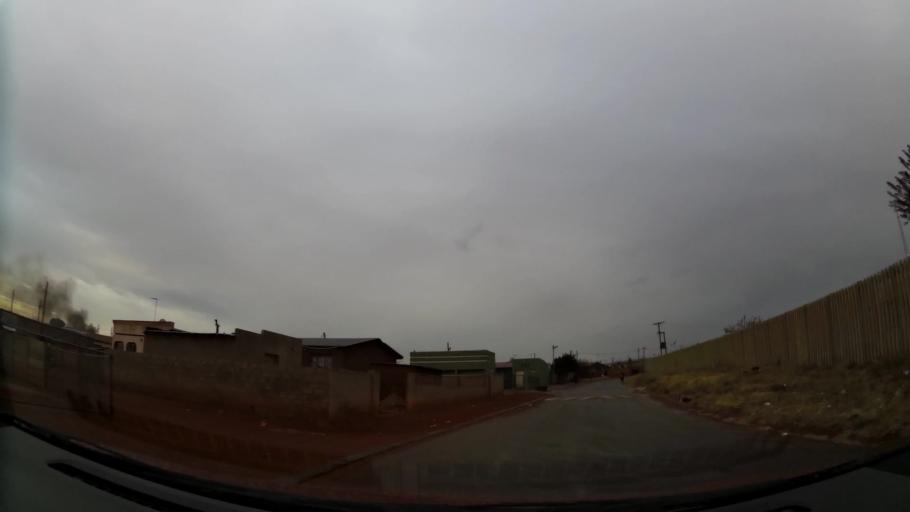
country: ZA
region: Gauteng
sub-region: West Rand District Municipality
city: Randfontein
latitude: -26.1731
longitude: 27.7840
